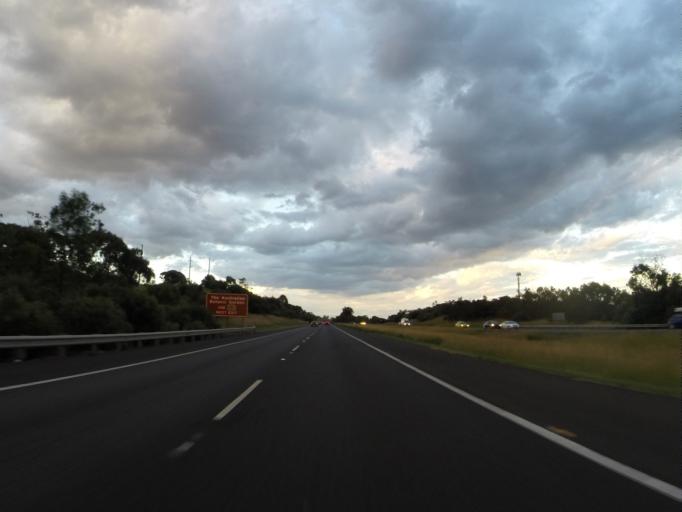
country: AU
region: New South Wales
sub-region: Campbelltown Municipality
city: Glen Alpine
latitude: -34.0766
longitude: 150.7746
